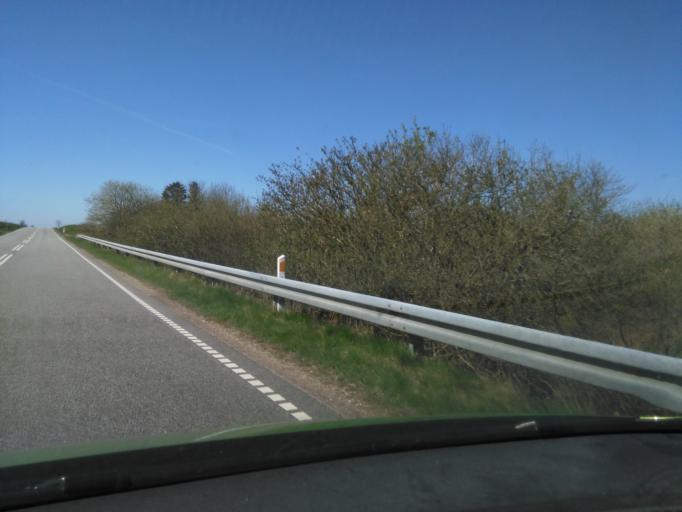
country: DK
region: South Denmark
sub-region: Billund Kommune
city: Grindsted
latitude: 55.6964
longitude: 8.9431
